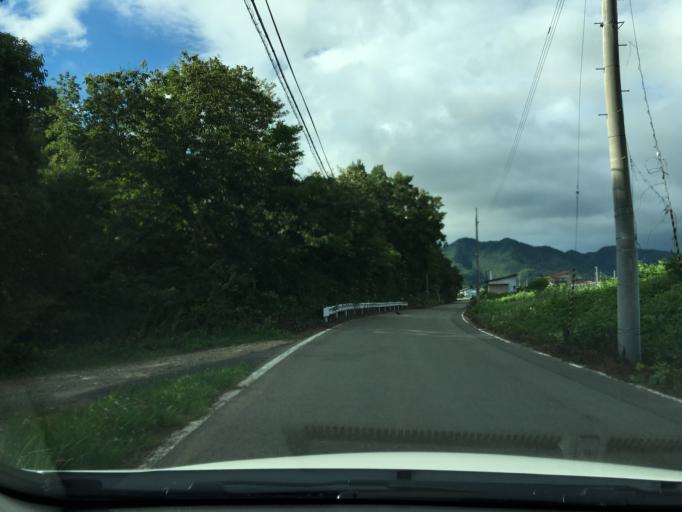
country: JP
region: Yamagata
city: Takahata
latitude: 37.9347
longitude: 140.2031
